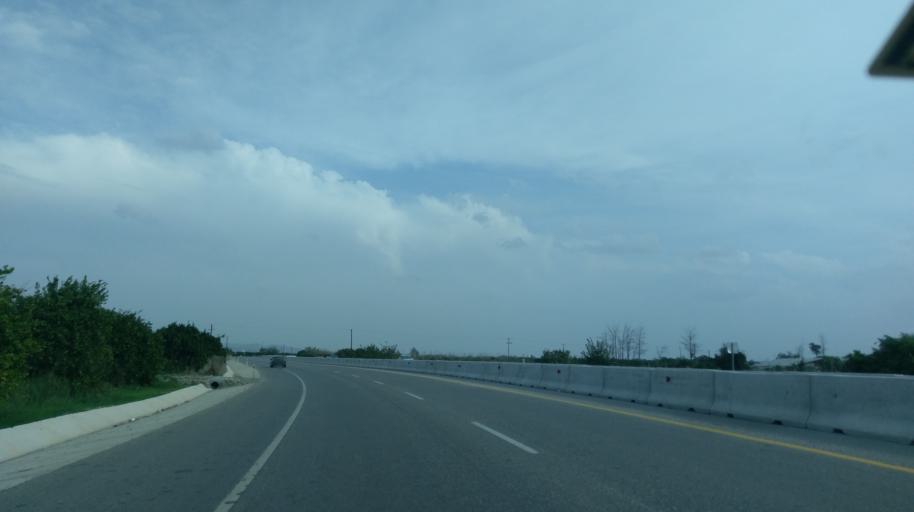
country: CY
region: Lefkosia
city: Morfou
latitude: 35.1973
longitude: 33.0169
